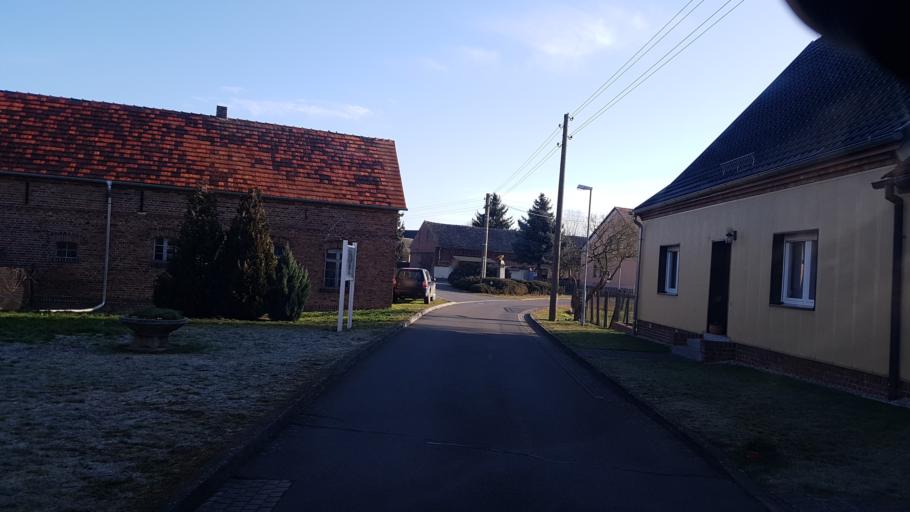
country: DE
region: Brandenburg
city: Lubbenau
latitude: 51.8173
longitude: 13.9037
